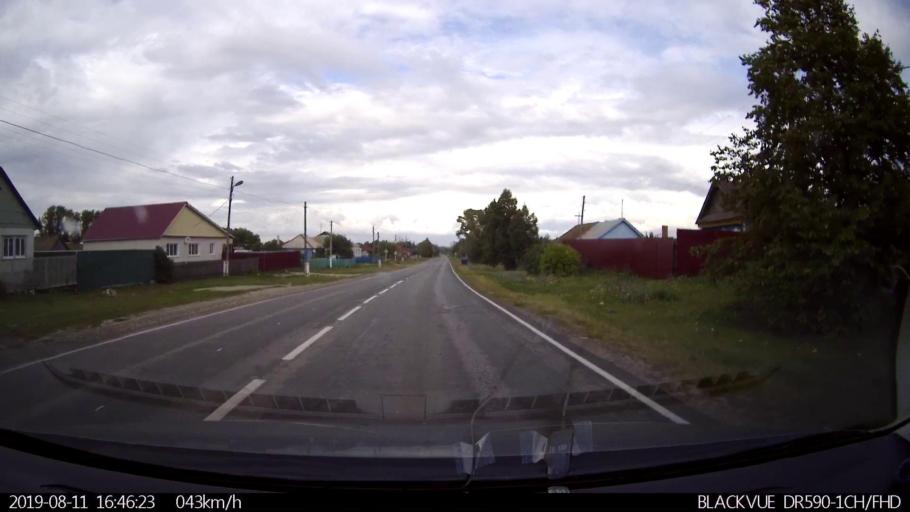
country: RU
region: Ulyanovsk
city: Mayna
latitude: 54.1977
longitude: 47.6880
